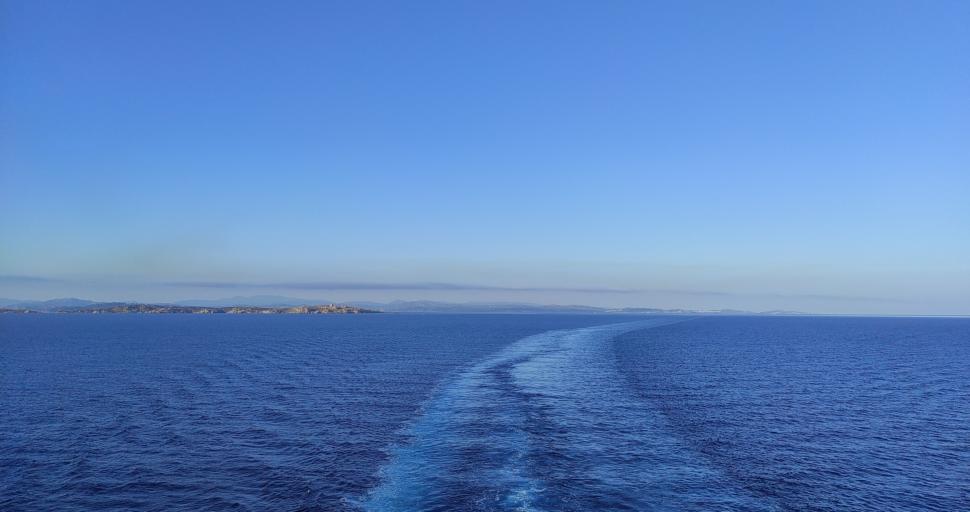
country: IT
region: Sardinia
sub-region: Provincia di Olbia-Tempio
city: La Maddalena
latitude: 41.3512
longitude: 9.3620
